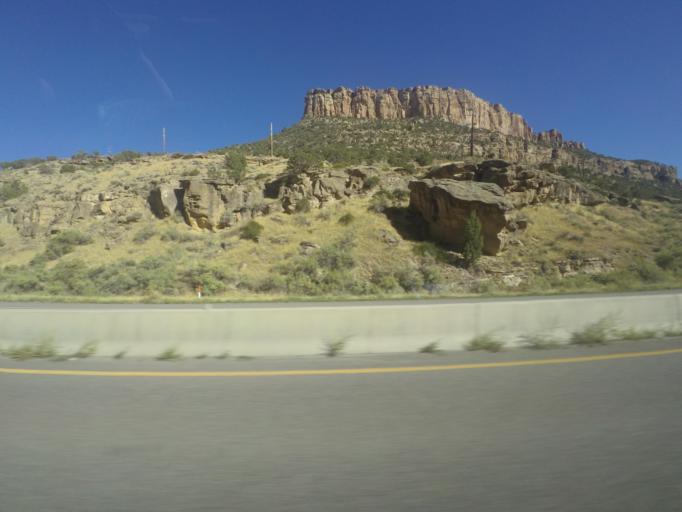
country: US
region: Colorado
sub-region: Mesa County
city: Palisade
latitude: 39.1944
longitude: -108.2817
